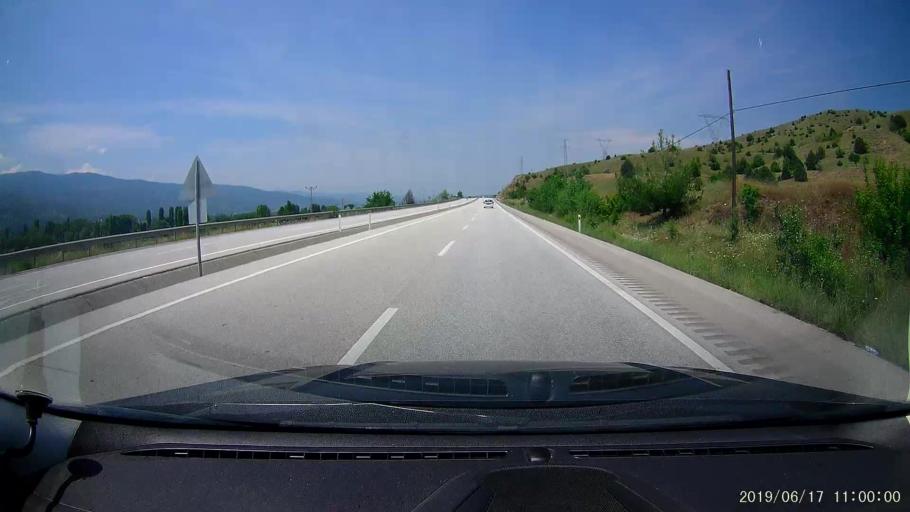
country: TR
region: Kastamonu
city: Tosya
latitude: 41.0380
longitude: 34.1917
